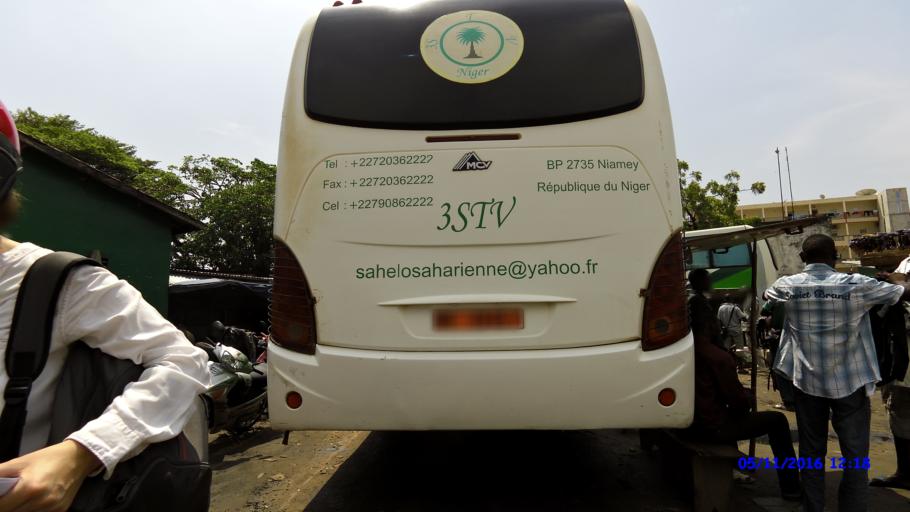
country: BJ
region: Littoral
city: Cotonou
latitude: 6.3588
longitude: 2.4242
